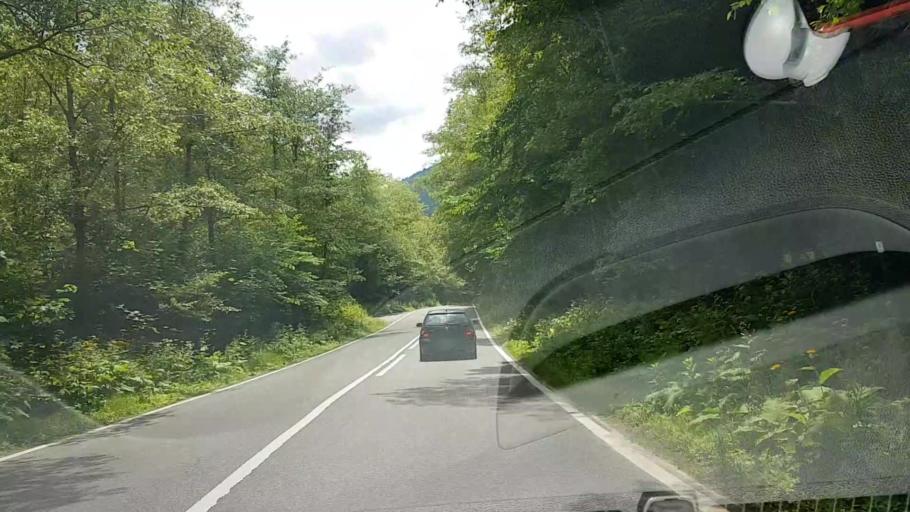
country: RO
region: Suceava
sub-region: Comuna Crucea
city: Crucea
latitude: 47.2980
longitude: 25.6322
